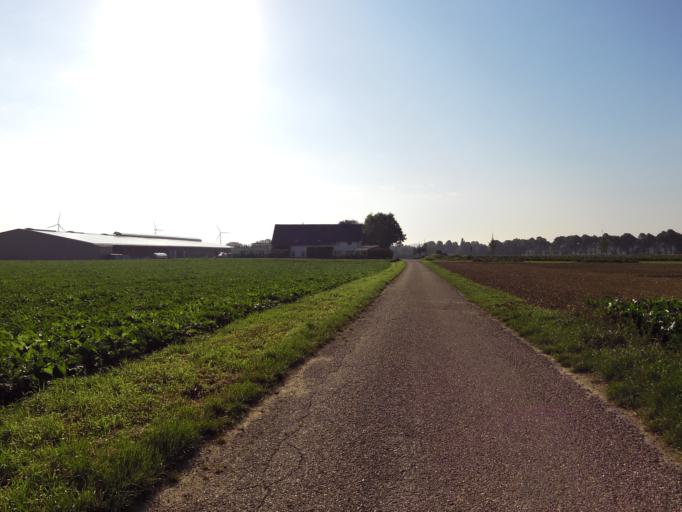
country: DE
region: North Rhine-Westphalia
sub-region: Regierungsbezirk Koln
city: Alsdorf
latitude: 50.9017
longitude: 6.1408
